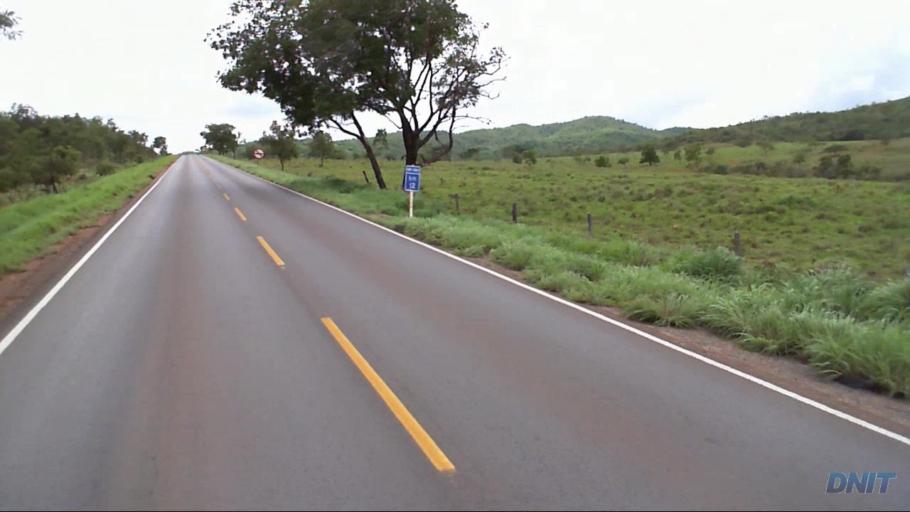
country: BR
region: Goias
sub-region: Padre Bernardo
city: Padre Bernardo
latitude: -15.4419
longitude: -48.1978
